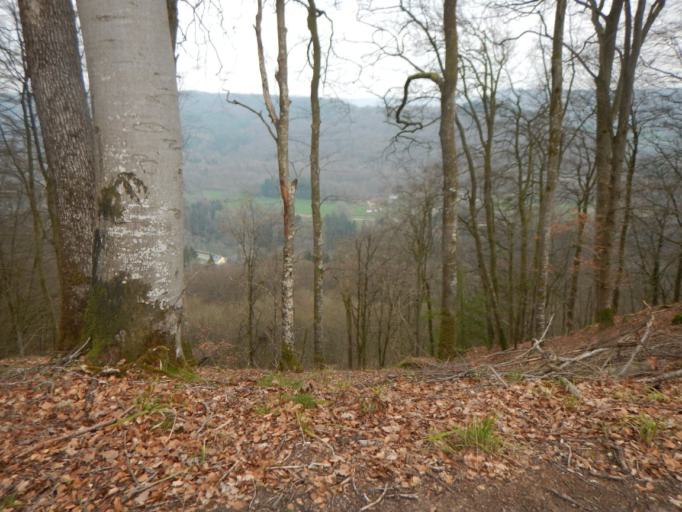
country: LU
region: Grevenmacher
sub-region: Canton d'Echternach
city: Beaufort
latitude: 49.8406
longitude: 6.3138
